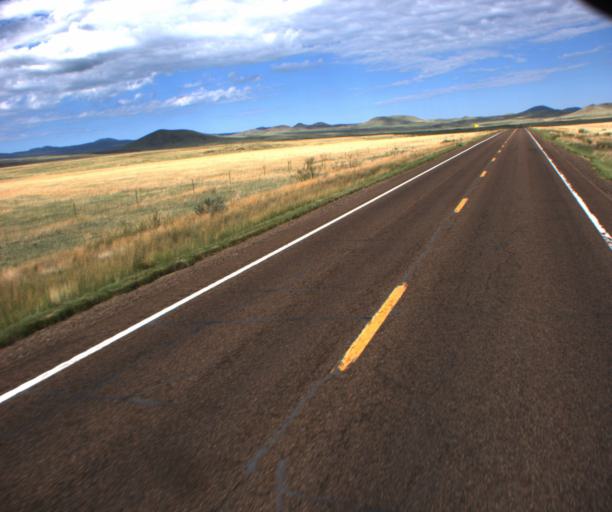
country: US
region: Arizona
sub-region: Apache County
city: Springerville
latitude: 34.1923
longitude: -109.3604
